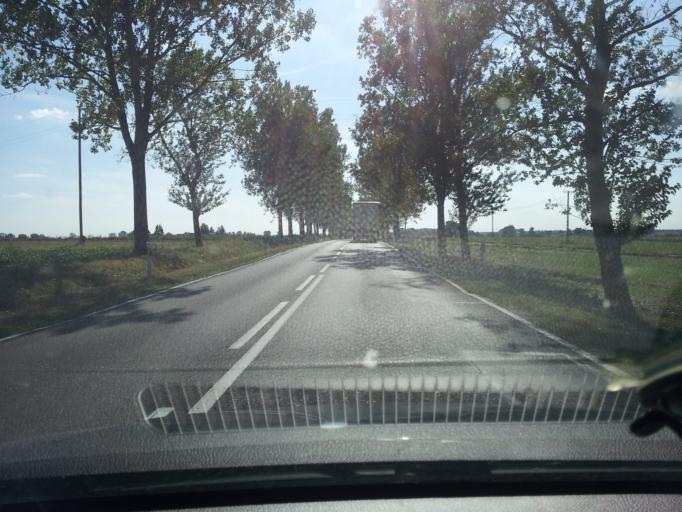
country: PL
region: Kujawsko-Pomorskie
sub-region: Powiat golubsko-dobrzynski
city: Kowalewo Pomorskie
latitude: 53.1421
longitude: 18.8637
